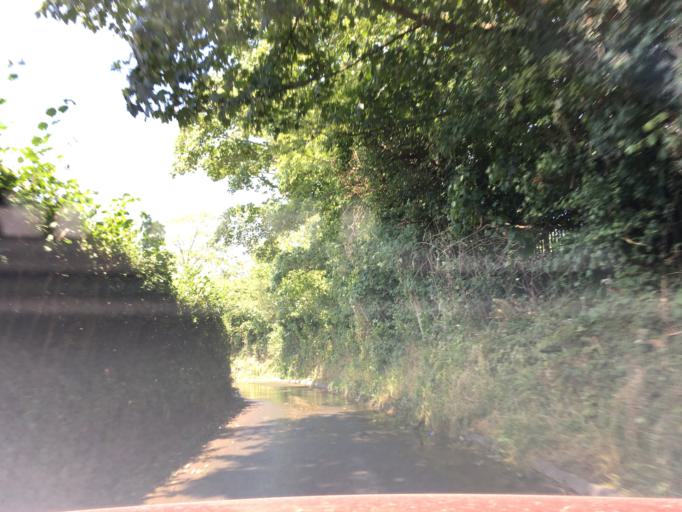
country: GB
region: Wales
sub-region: Caerphilly County Borough
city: Machen
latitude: 51.5433
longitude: -3.1297
